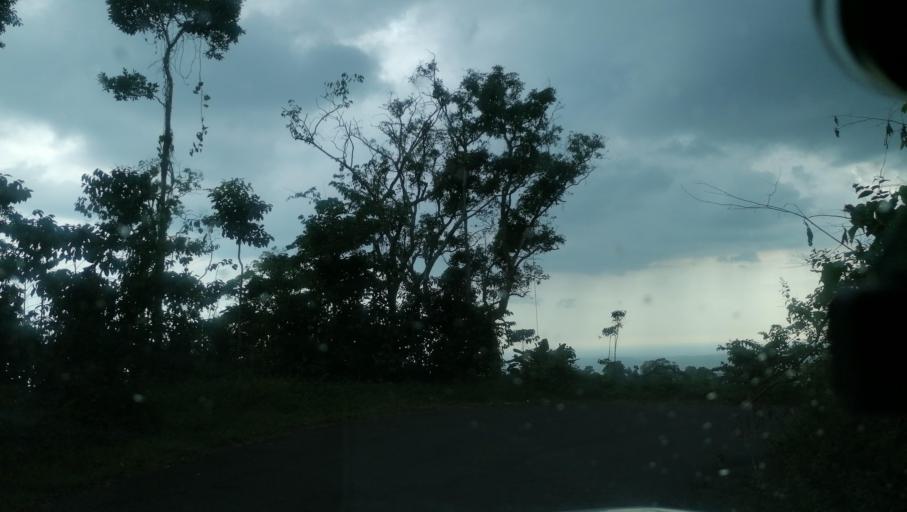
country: MX
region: Chiapas
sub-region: Cacahoatan
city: Benito Juarez
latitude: 15.0698
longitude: -92.1782
